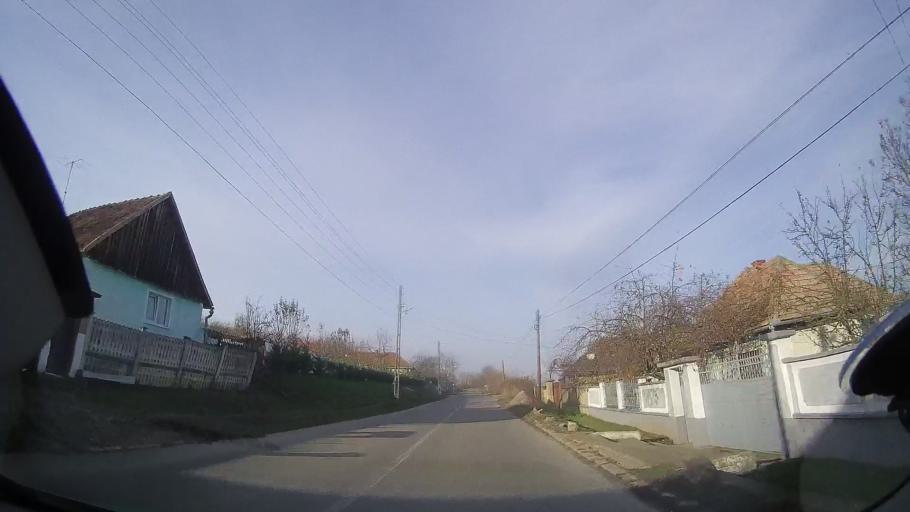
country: RO
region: Bihor
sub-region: Comuna Spinus
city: Spinus
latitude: 47.1818
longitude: 22.2108
